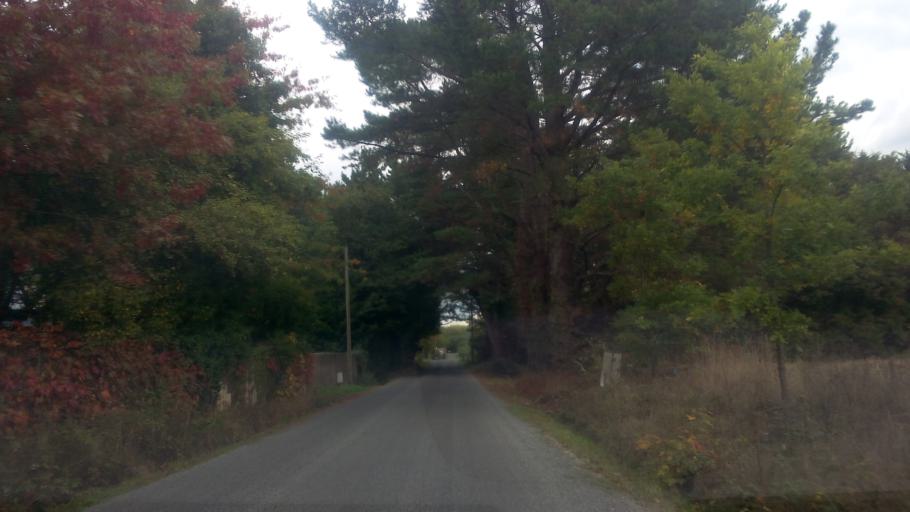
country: FR
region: Brittany
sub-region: Departement du Morbihan
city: Saint-Perreux
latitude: 47.6662
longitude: -2.1346
